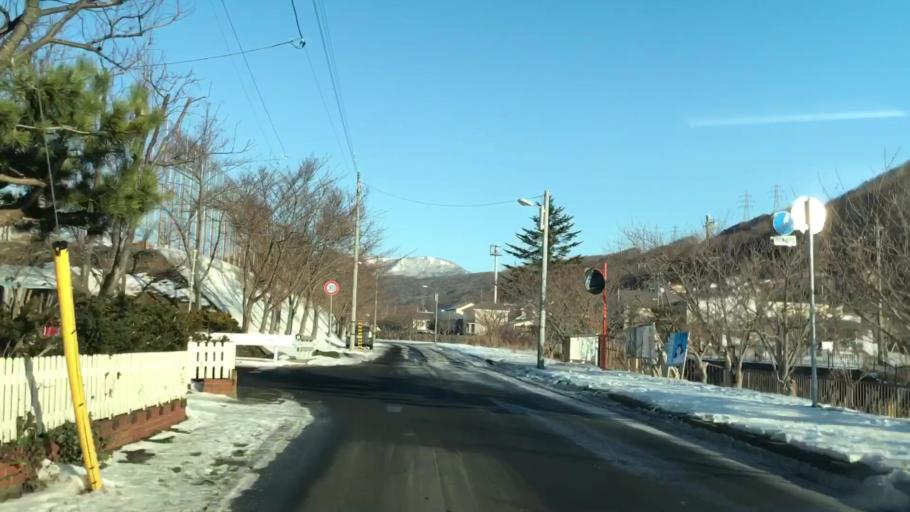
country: JP
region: Hokkaido
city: Muroran
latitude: 42.3676
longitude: 141.0382
